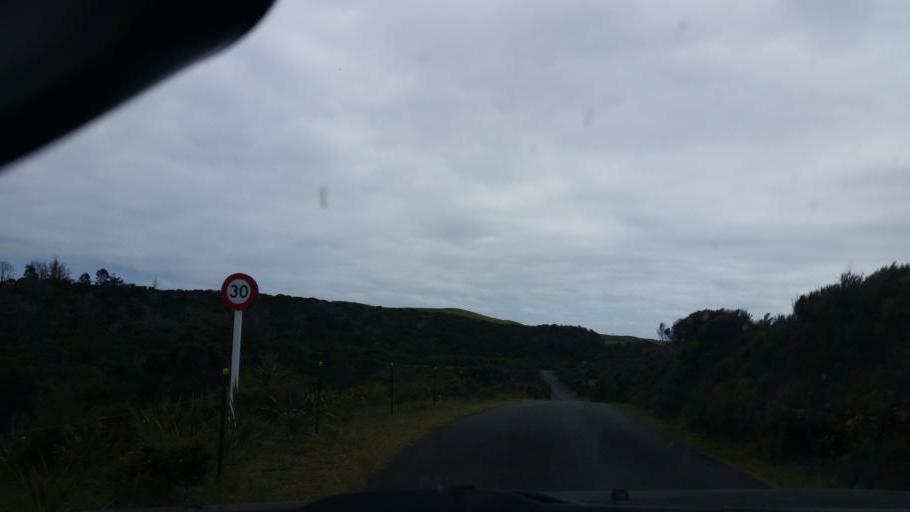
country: NZ
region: Northland
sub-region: Kaipara District
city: Dargaville
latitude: -35.8126
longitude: 173.6509
